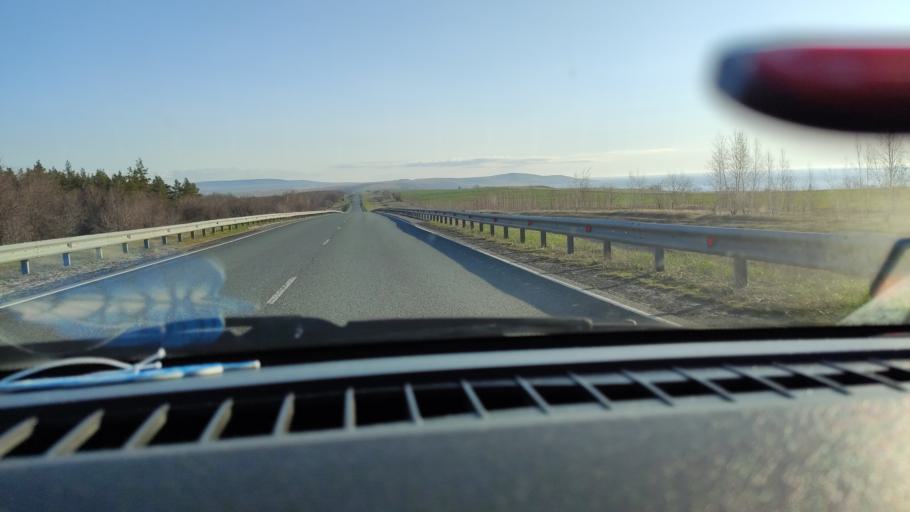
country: RU
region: Saratov
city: Balakovo
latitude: 52.1710
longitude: 47.8308
